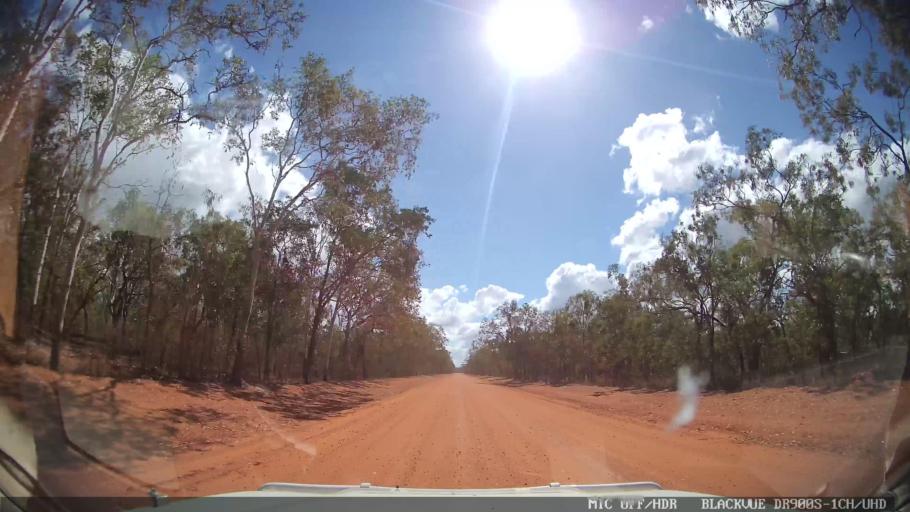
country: AU
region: Queensland
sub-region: Cook
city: Cooktown
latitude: -15.1977
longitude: 144.3836
